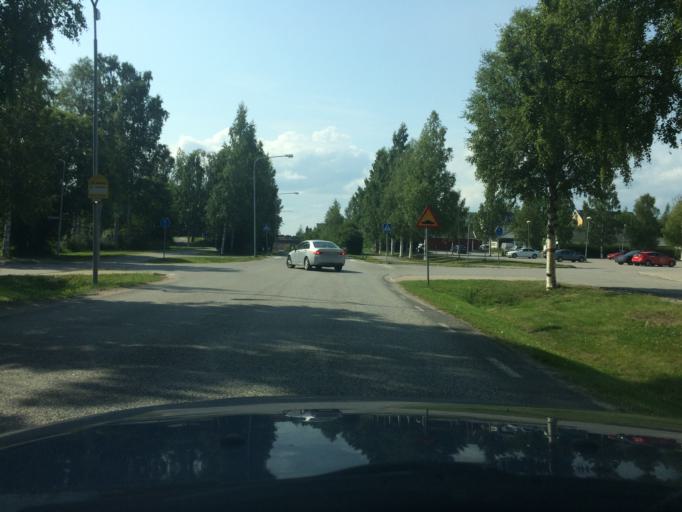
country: SE
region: Norrbotten
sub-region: Pitea Kommun
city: Pitea
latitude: 65.3234
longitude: 21.4774
